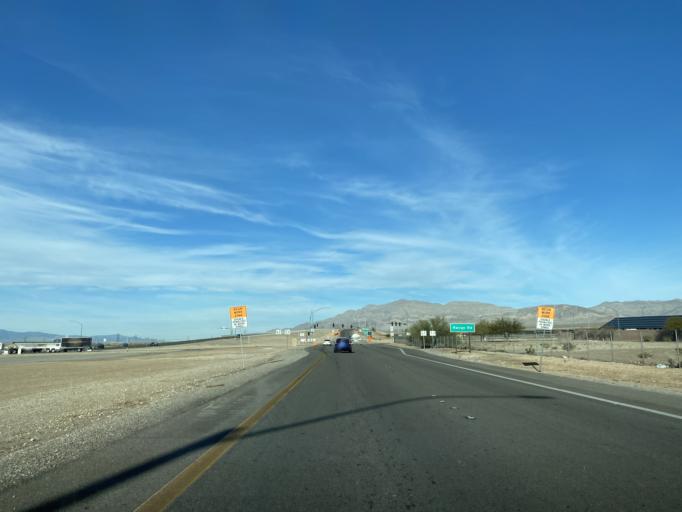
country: US
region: Nevada
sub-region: Clark County
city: Nellis Air Force Base
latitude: 36.2760
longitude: -115.0589
